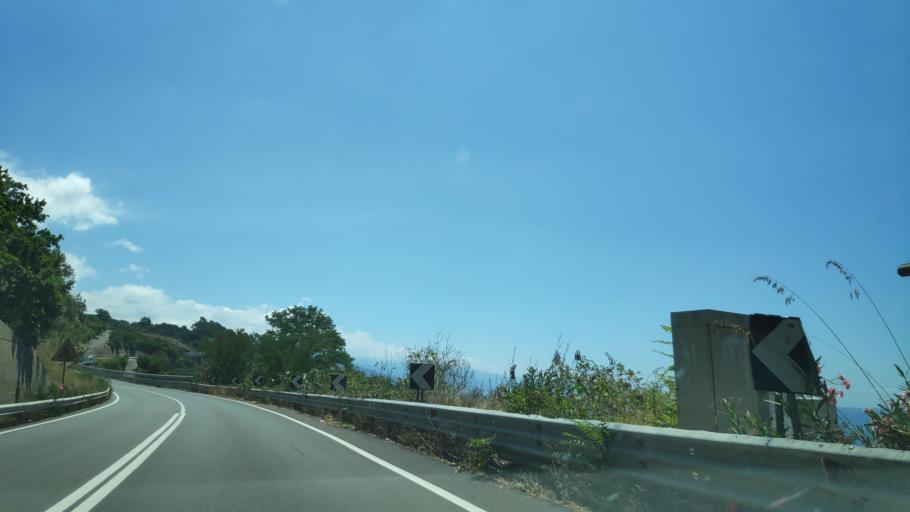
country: IT
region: Calabria
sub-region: Provincia di Cosenza
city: Cittadella del Capo
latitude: 39.5460
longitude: 15.8846
